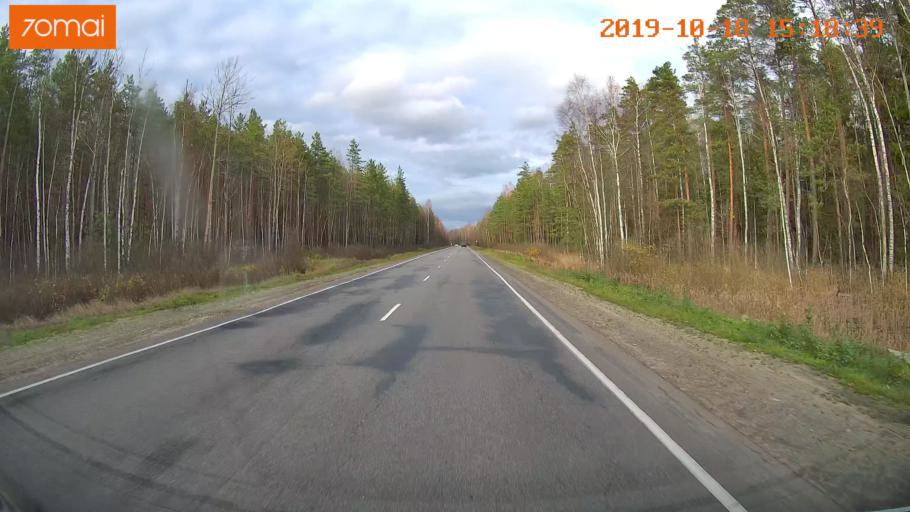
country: RU
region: Vladimir
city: Anopino
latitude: 55.6621
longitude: 40.7308
